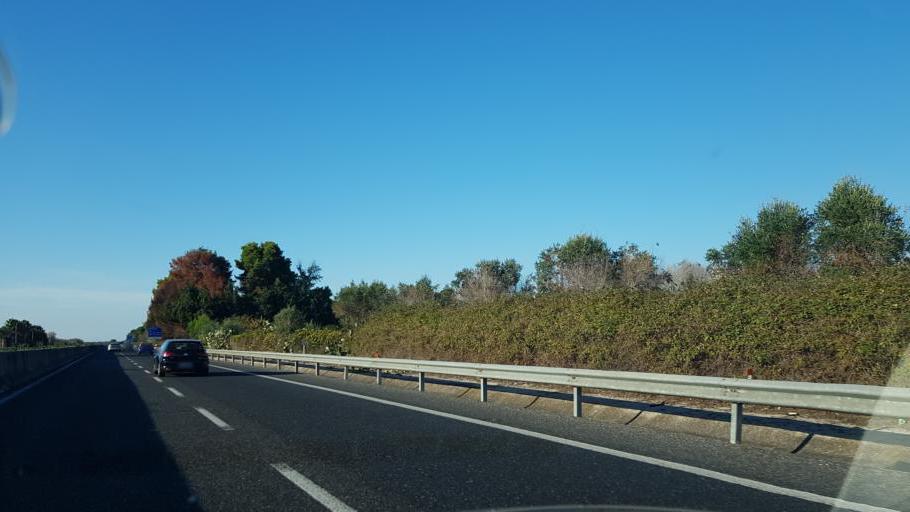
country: IT
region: Apulia
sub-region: Provincia di Brindisi
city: Torchiarolo
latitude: 40.4761
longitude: 18.0475
